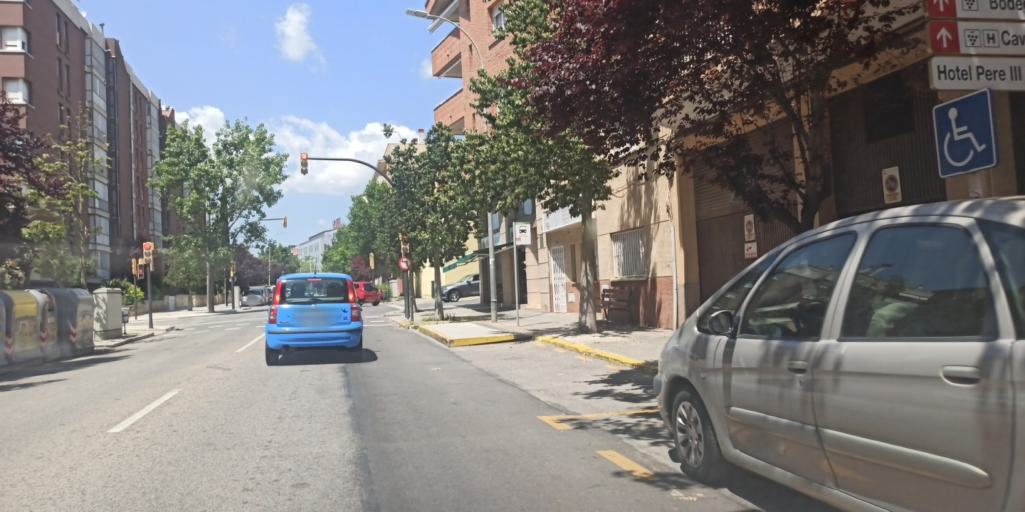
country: ES
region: Catalonia
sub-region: Provincia de Barcelona
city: Vilafranca del Penedes
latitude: 41.3397
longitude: 1.6950
